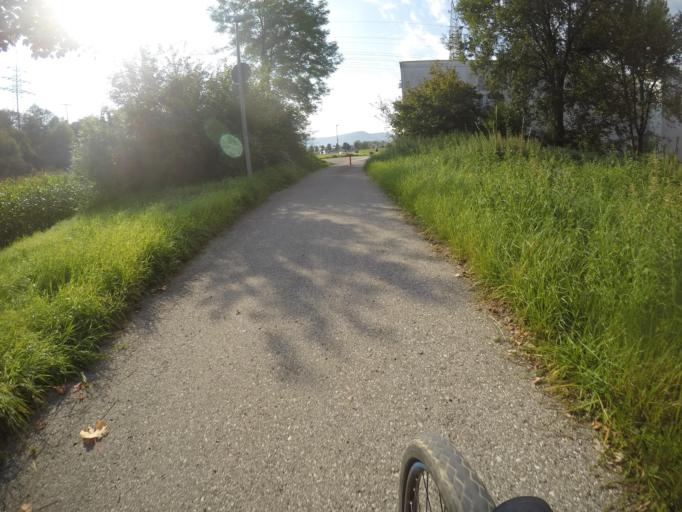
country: DE
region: Baden-Wuerttemberg
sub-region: Tuebingen Region
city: Riederich
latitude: 48.5508
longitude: 9.2761
